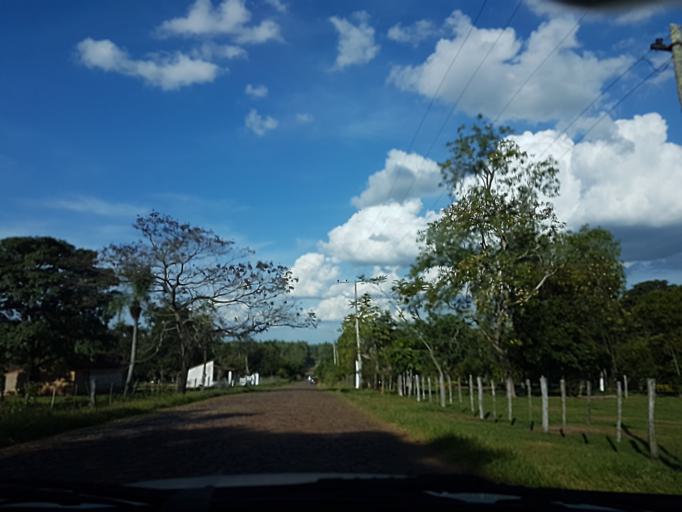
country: PY
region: Cordillera
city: Arroyos y Esteros
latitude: -24.9966
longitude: -57.1562
